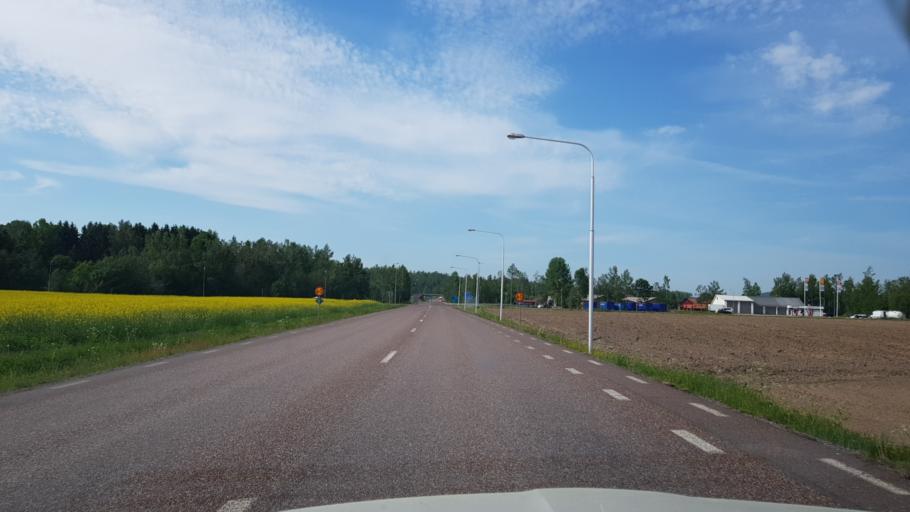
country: SE
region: Dalarna
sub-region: Borlange Kommun
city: Ornas
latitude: 60.4164
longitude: 15.5965
